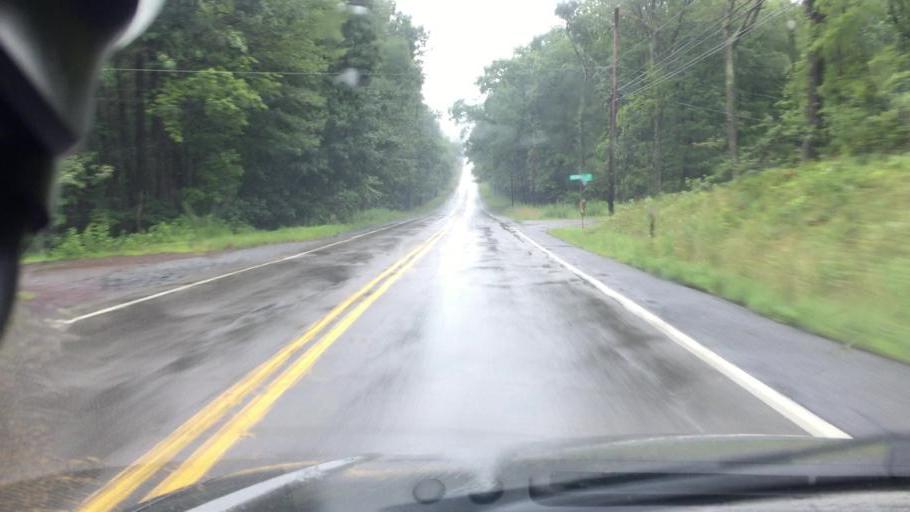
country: US
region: Pennsylvania
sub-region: Luzerne County
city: Freeland
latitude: 41.0277
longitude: -75.8589
